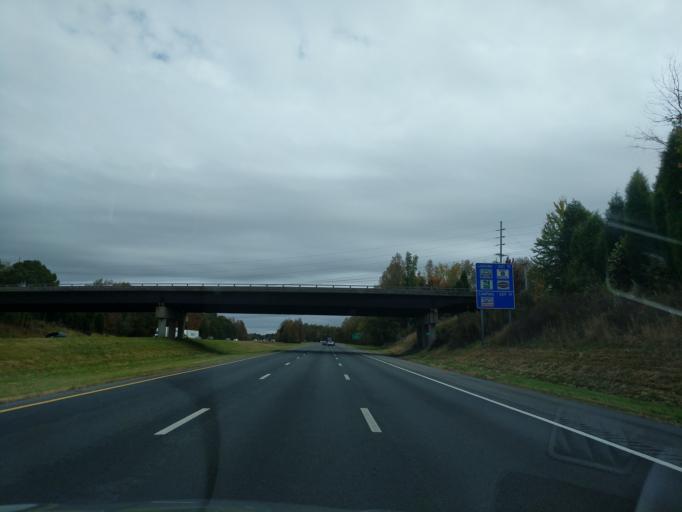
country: US
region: North Carolina
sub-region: Davidson County
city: Lexington
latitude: 35.7766
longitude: -80.2800
